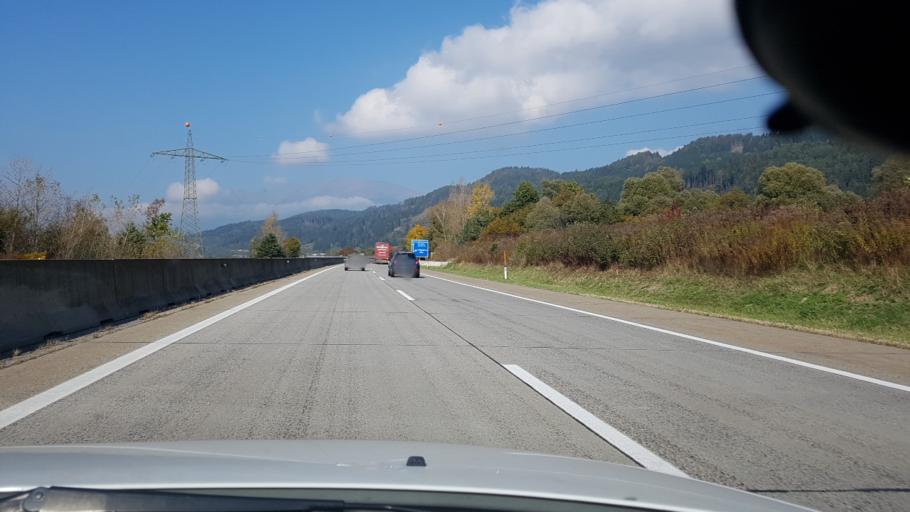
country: AT
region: Carinthia
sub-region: Politischer Bezirk Spittal an der Drau
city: Millstatt
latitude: 46.7693
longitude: 13.5545
